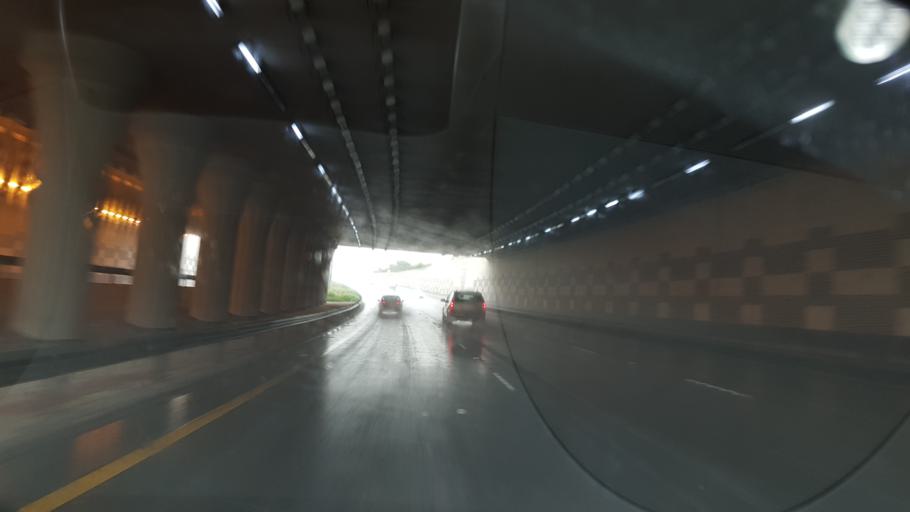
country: BH
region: Central Governorate
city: Madinat Hamad
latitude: 26.0982
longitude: 50.5114
